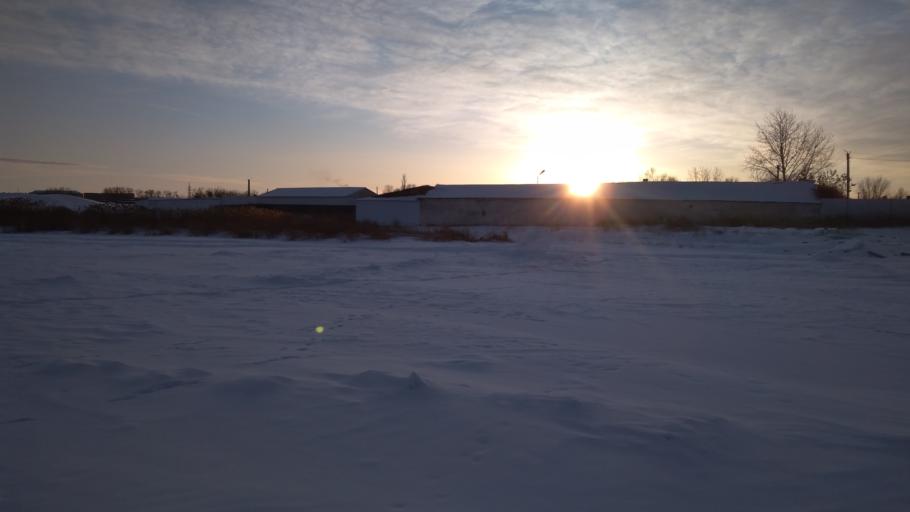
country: RU
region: Chelyabinsk
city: Troitsk
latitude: 54.0874
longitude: 61.5848
